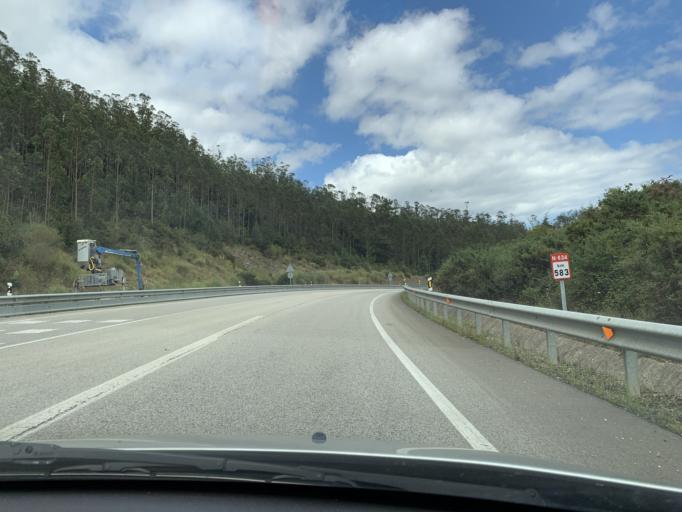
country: ES
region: Galicia
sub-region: Provincia de Lugo
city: Mondonedo
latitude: 43.4588
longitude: -7.3220
